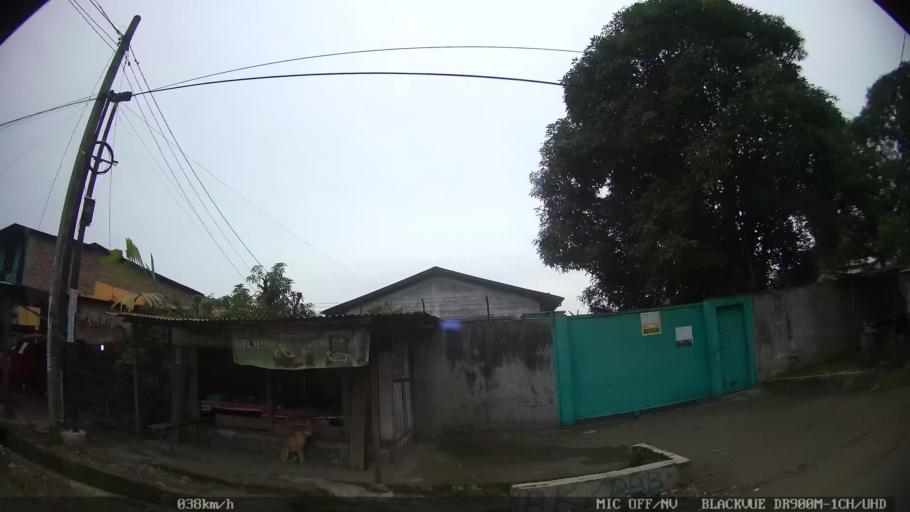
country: ID
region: North Sumatra
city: Deli Tua
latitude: 3.5369
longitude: 98.7341
